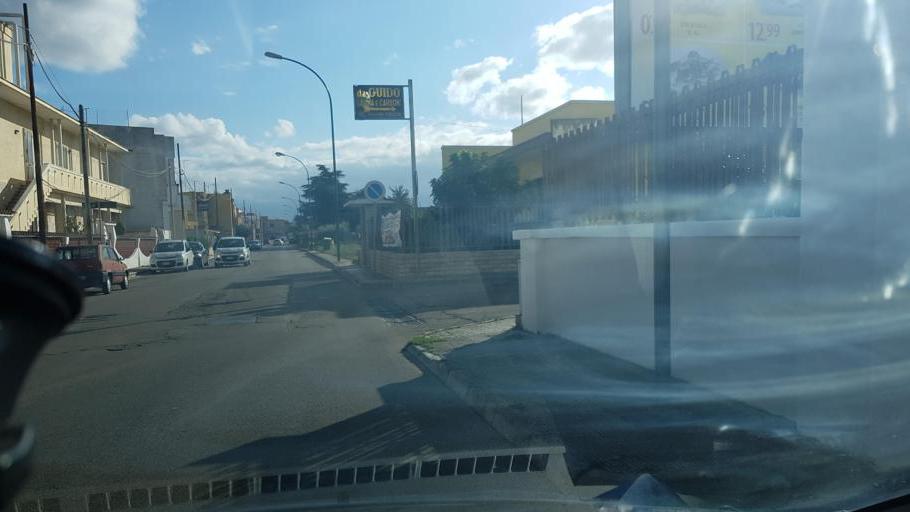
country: IT
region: Apulia
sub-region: Provincia di Lecce
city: Squinzano
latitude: 40.4352
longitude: 18.0318
